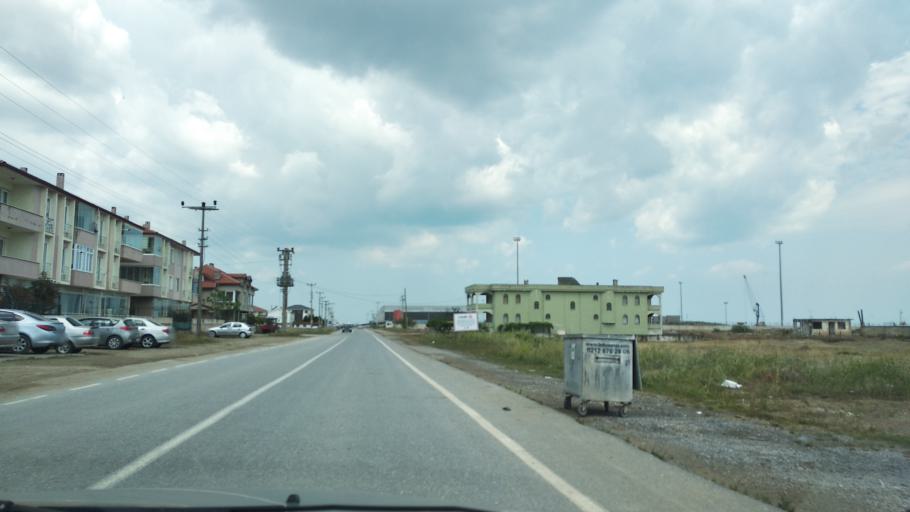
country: TR
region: Sakarya
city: Karasu
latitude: 41.1153
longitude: 30.6788
